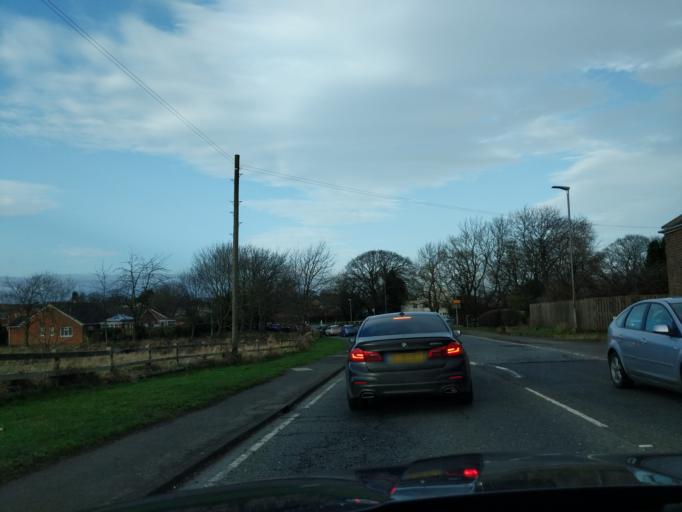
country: GB
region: England
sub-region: Northumberland
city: Ponteland
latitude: 55.0489
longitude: -1.7343
